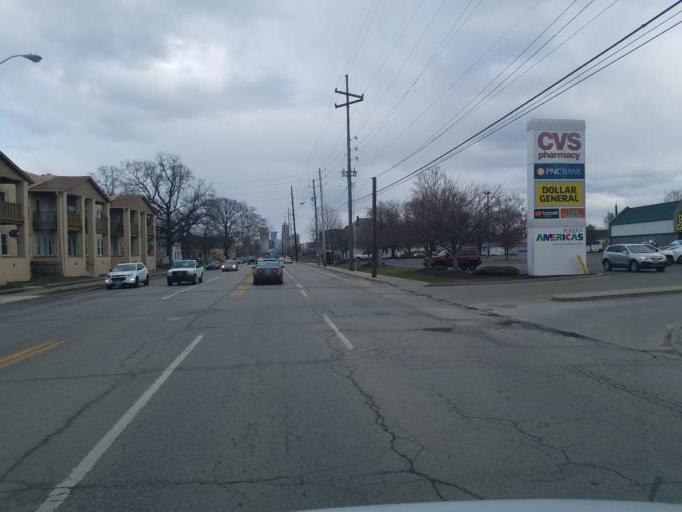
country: US
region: Indiana
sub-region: Marion County
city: Indianapolis
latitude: 39.7663
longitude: -86.1957
